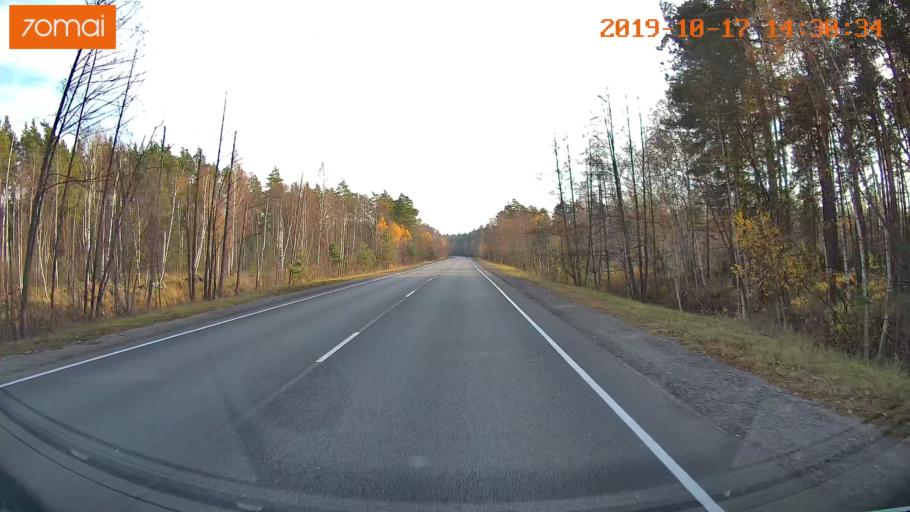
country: RU
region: Rjazan
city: Solotcha
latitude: 54.9461
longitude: 39.9474
